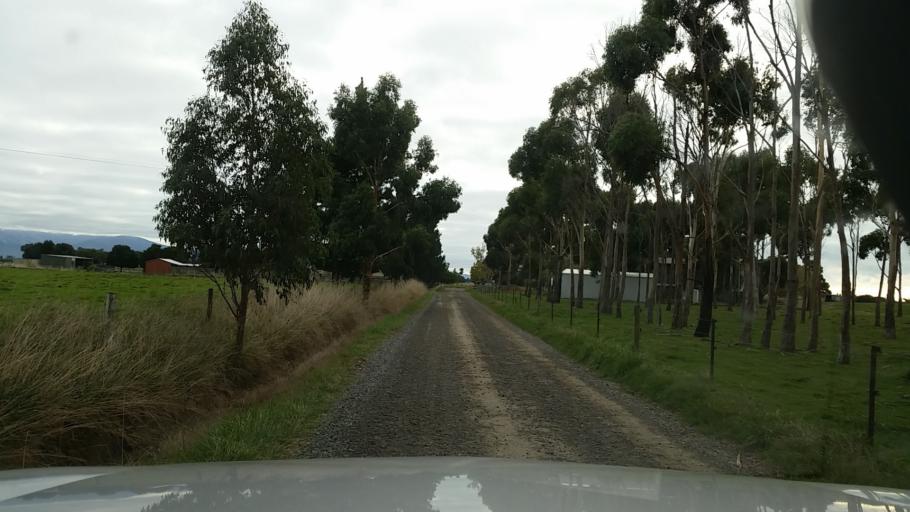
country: NZ
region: Marlborough
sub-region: Marlborough District
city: Blenheim
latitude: -41.5209
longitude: 174.0391
